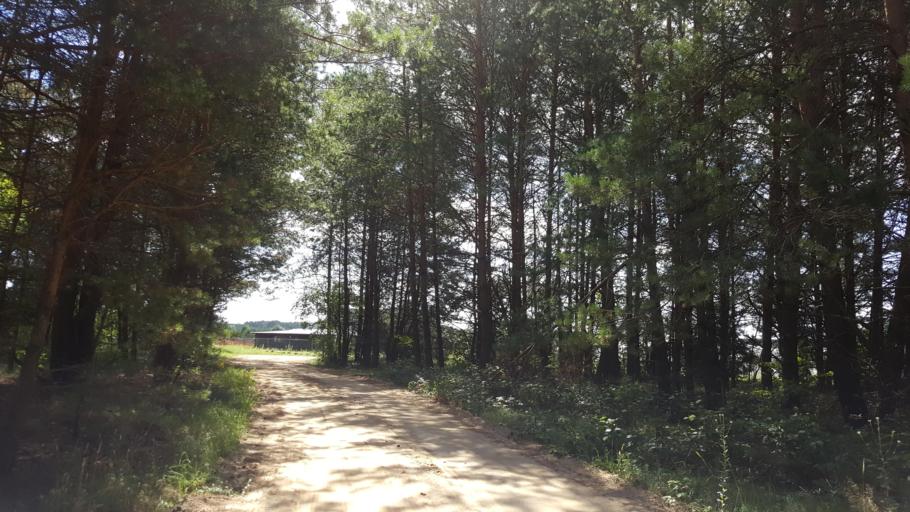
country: BY
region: Brest
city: Zhabinka
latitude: 52.3973
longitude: 24.0635
